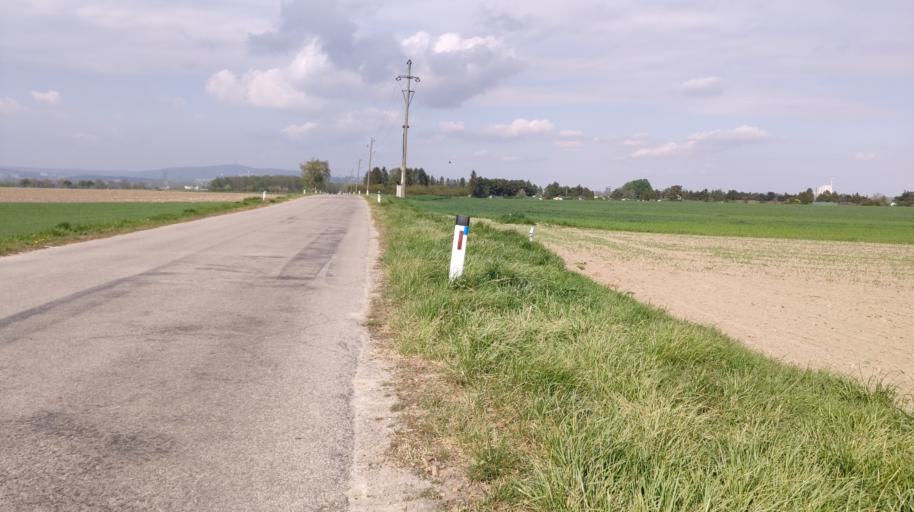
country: AT
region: Lower Austria
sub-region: Politischer Bezirk Bruck an der Leitha
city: Berg
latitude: 48.1082
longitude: 17.0501
